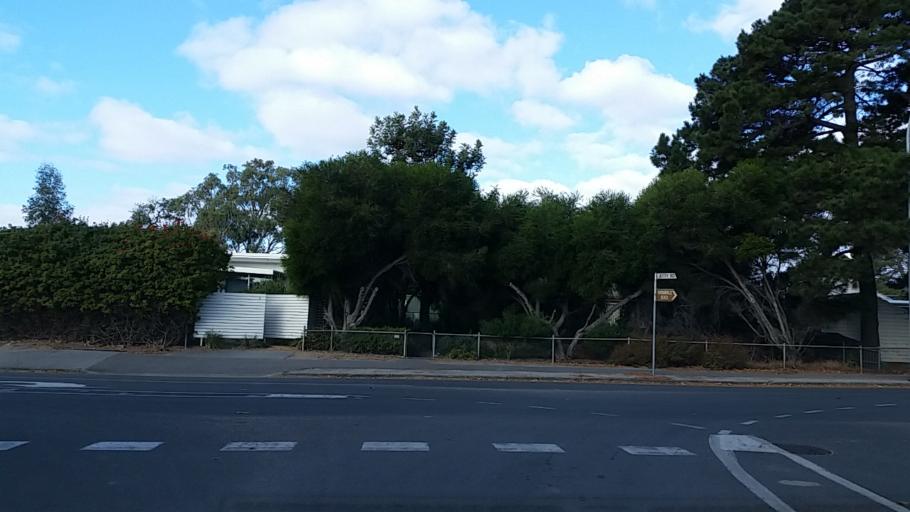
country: AU
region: South Australia
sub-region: Yankalilla
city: Normanville
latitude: -35.4447
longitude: 138.3160
